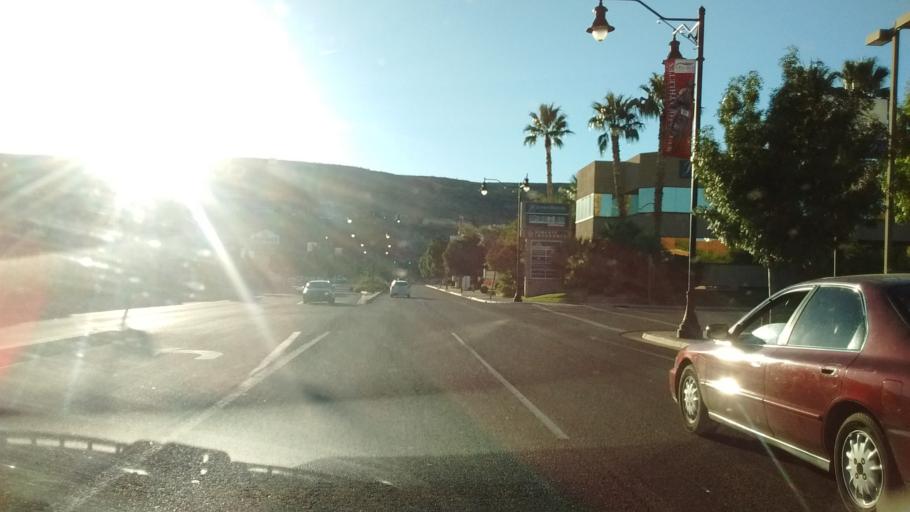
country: US
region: Utah
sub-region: Washington County
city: Saint George
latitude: 37.1099
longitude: -113.5872
